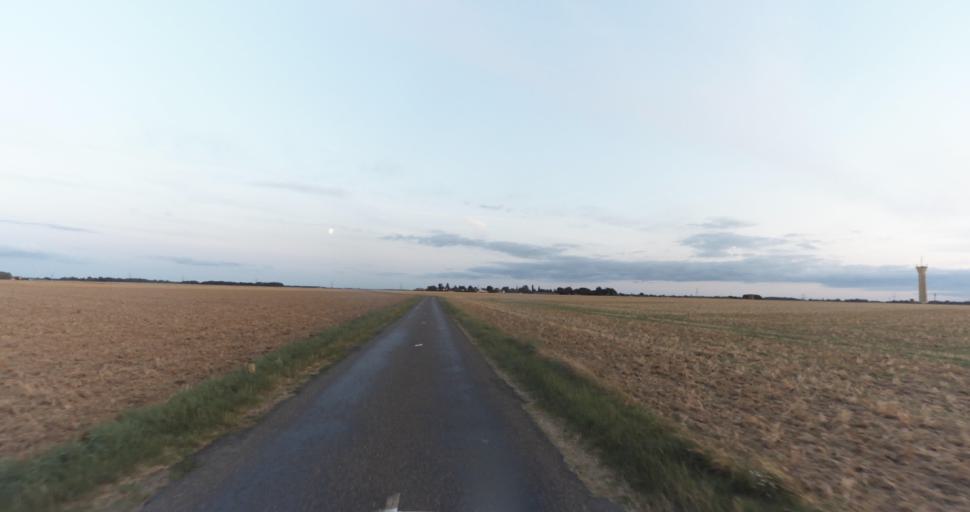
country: FR
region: Haute-Normandie
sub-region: Departement de l'Eure
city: La Madeleine-de-Nonancourt
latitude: 48.8769
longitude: 1.2433
